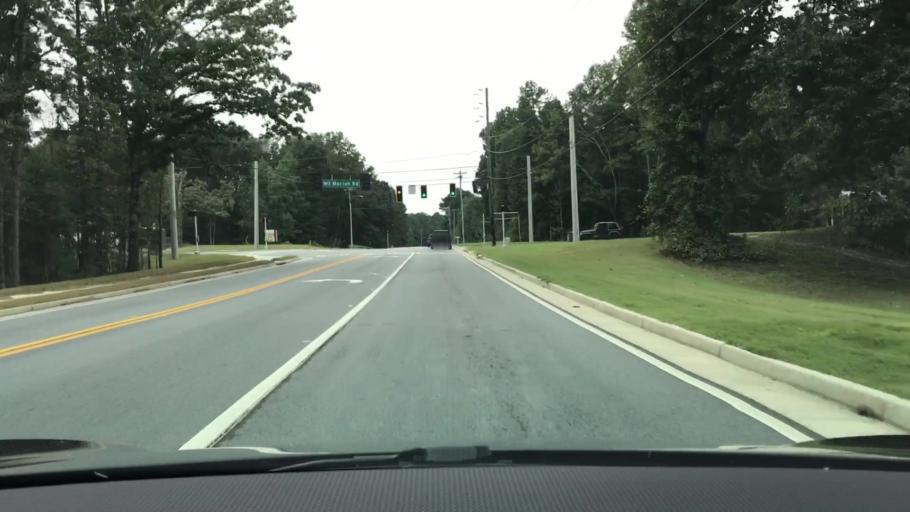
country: US
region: Georgia
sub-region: Barrow County
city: Auburn
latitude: 34.0717
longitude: -83.8560
